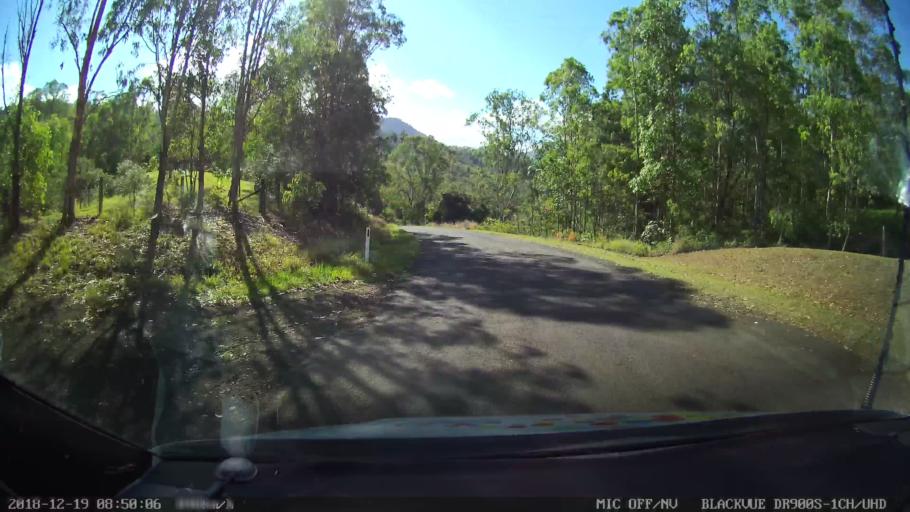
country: AU
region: New South Wales
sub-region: Kyogle
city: Kyogle
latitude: -28.3793
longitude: 152.9740
